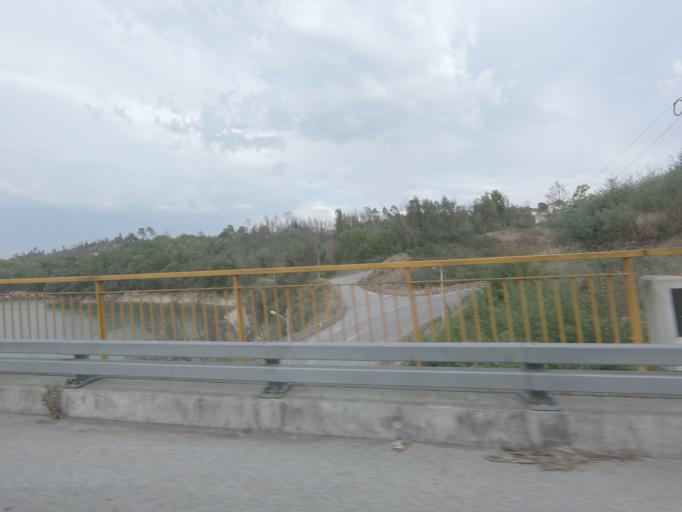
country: PT
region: Viseu
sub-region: Santa Comba Dao
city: Santa Comba Dao
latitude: 40.3922
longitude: -8.1278
